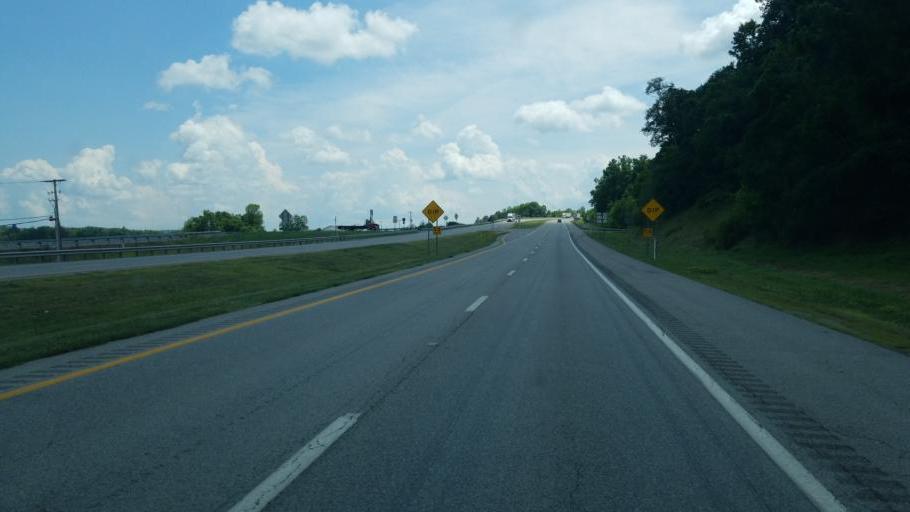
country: US
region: West Virginia
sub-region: Mason County
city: Point Pleasant
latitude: 38.8139
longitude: -82.1111
